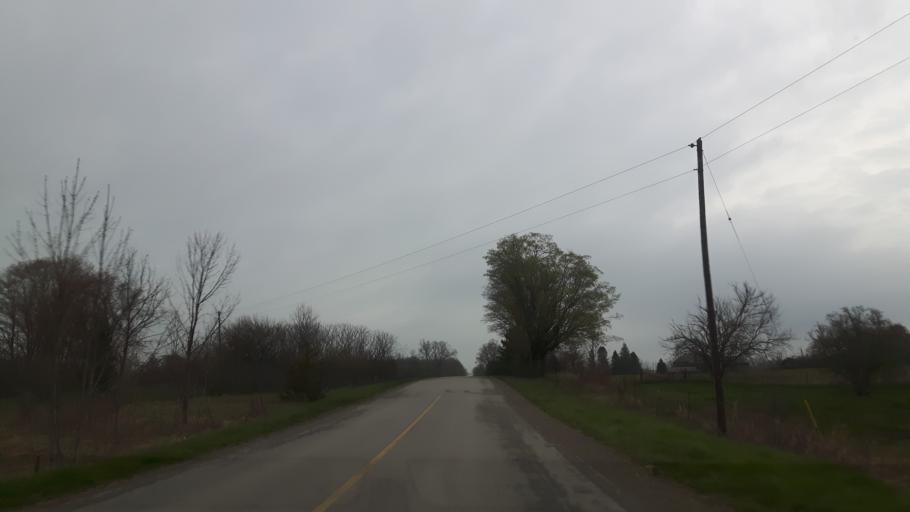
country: CA
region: Ontario
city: Bluewater
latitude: 43.5341
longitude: -81.6734
